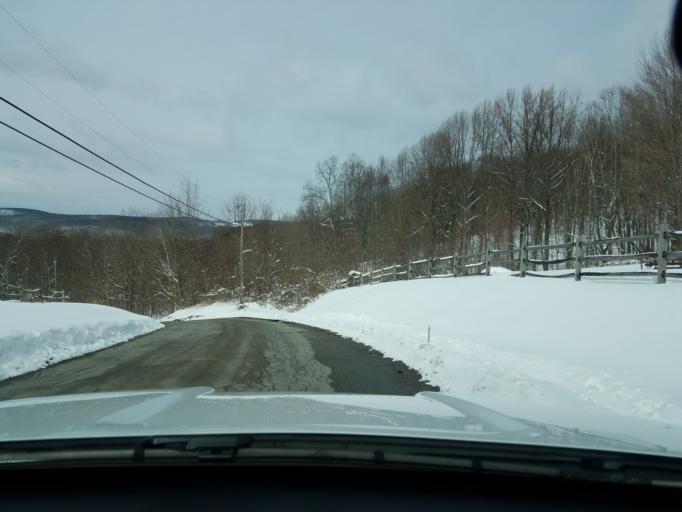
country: US
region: Connecticut
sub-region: Litchfield County
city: Kent
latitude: 41.7641
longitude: -73.4019
